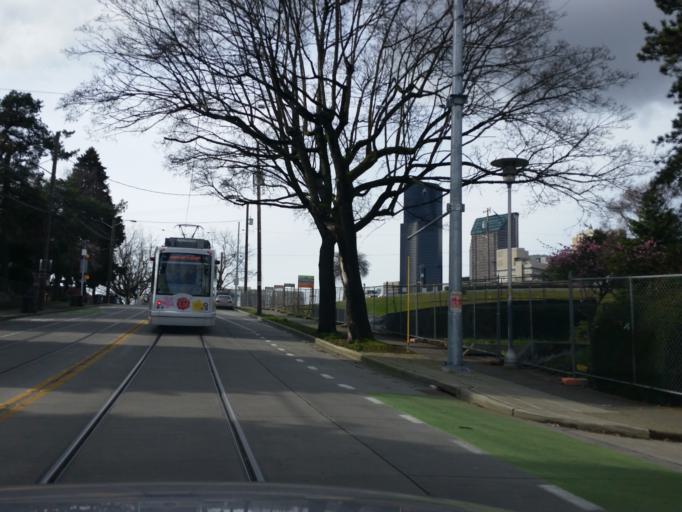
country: US
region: Washington
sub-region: King County
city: Seattle
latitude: 47.6018
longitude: -122.3179
